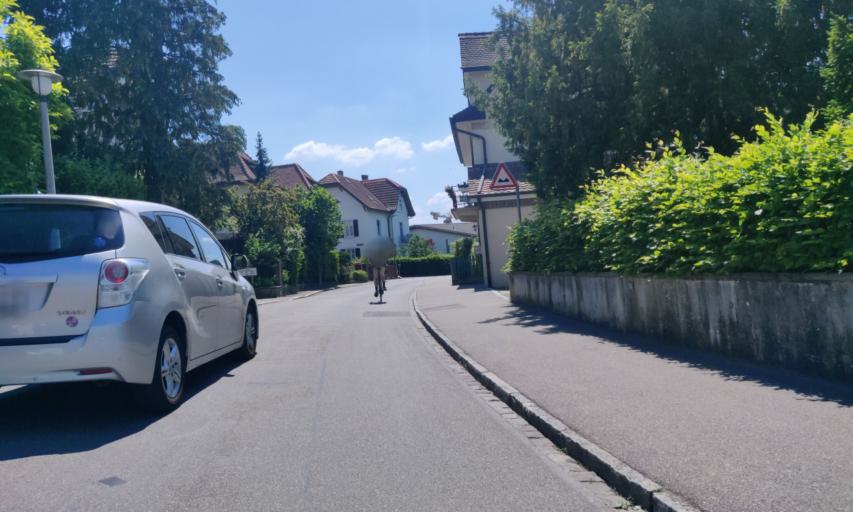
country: CH
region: Basel-Landschaft
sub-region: Bezirk Arlesheim
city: Munchenstein
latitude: 47.5260
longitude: 7.6187
